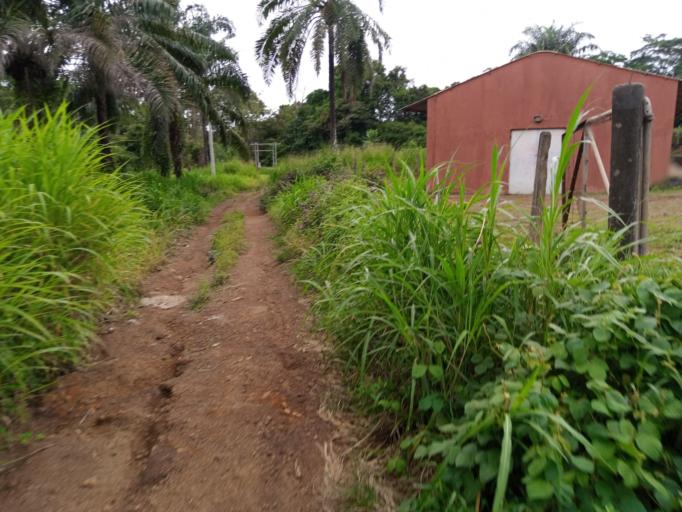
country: SL
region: Southern Province
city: Moyamba
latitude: 8.1668
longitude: -12.4289
